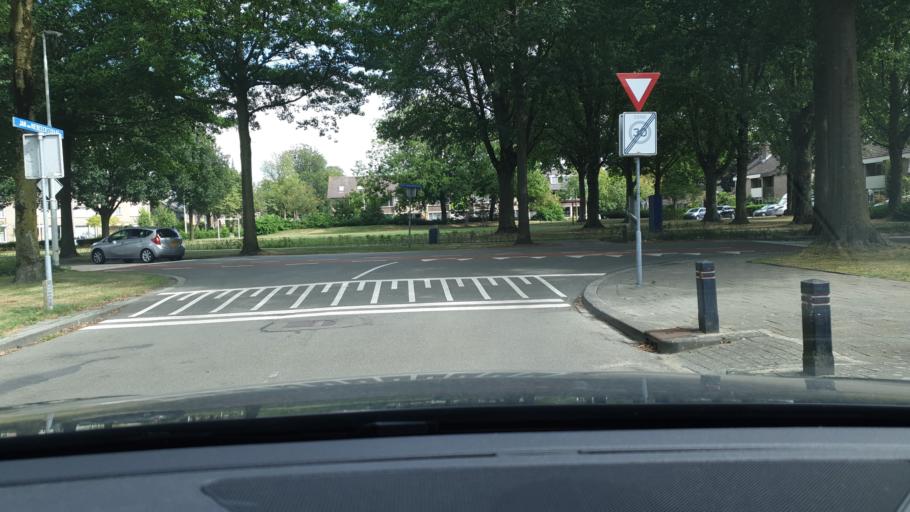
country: NL
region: North Brabant
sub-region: Gemeente Best
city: Best
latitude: 51.5077
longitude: 5.3847
